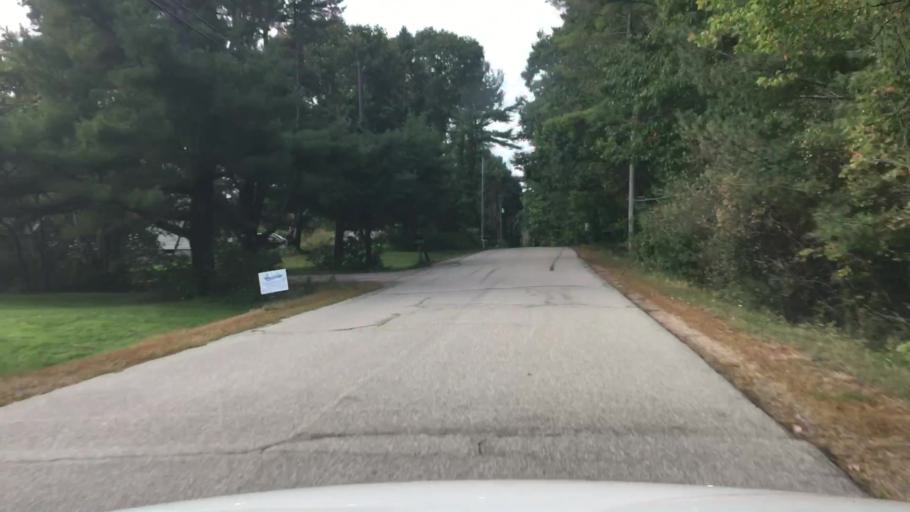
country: US
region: Maine
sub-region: York County
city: Kittery Point
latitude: 43.1019
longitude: -70.6999
